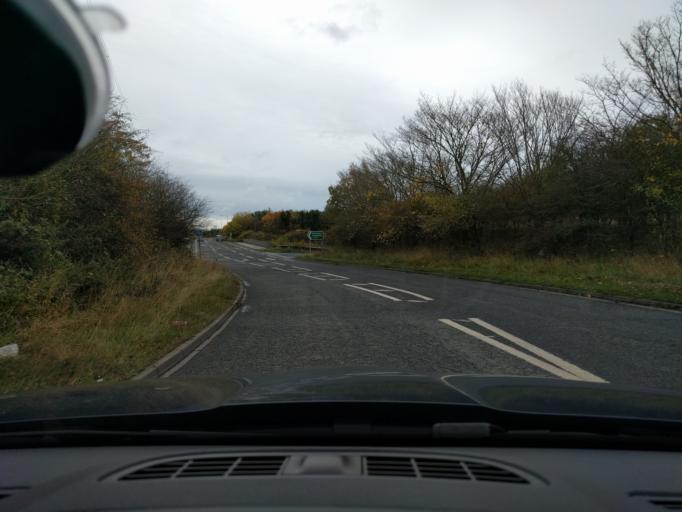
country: GB
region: England
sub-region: Northumberland
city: Ashington
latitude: 55.1478
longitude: -1.5525
